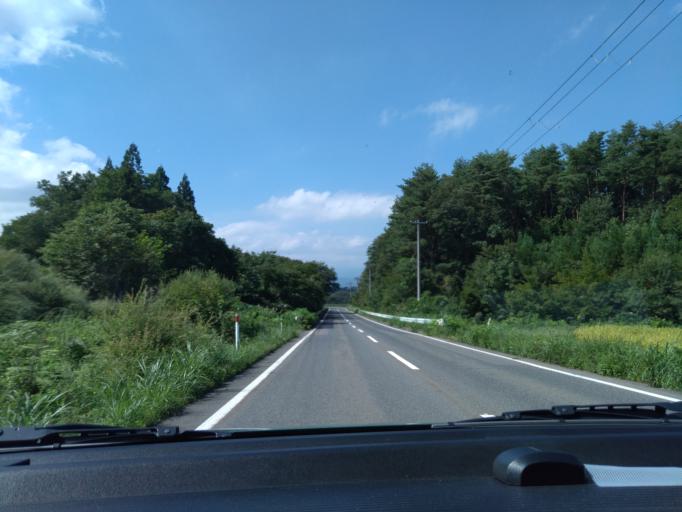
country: JP
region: Iwate
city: Shizukuishi
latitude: 39.6418
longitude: 141.0038
